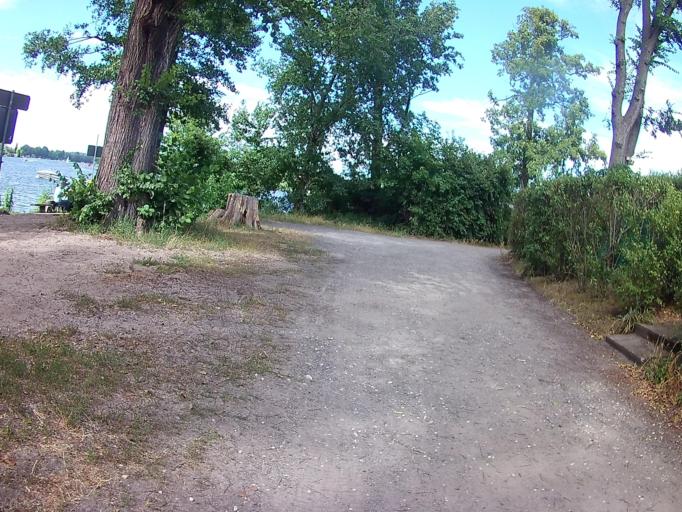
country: DE
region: Berlin
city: Schmockwitz
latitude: 52.3760
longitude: 13.6559
